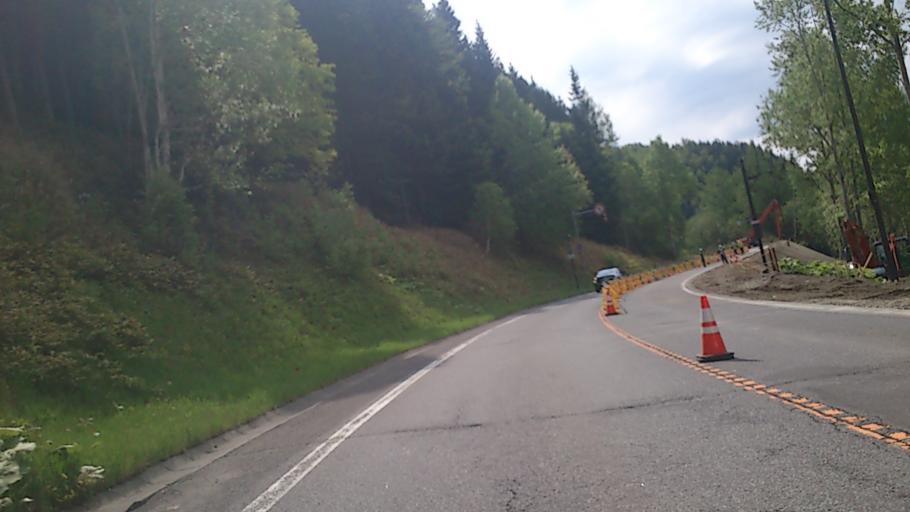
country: JP
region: Hokkaido
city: Kamikawa
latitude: 43.6847
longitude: 143.0319
